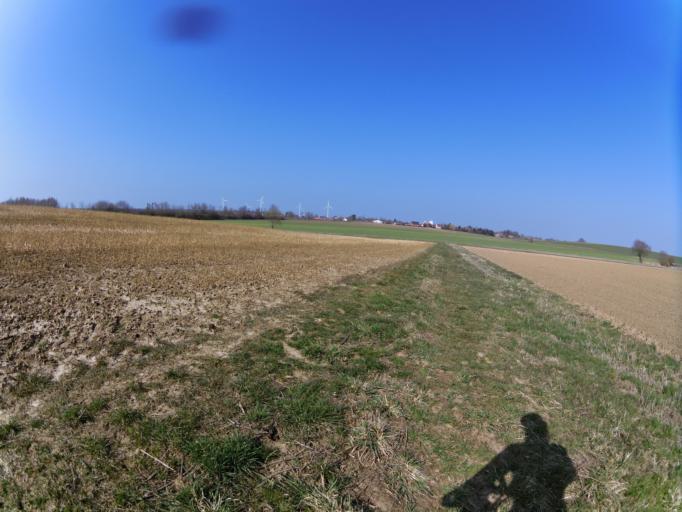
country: DE
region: Bavaria
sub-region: Regierungsbezirk Unterfranken
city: Geroldshausen
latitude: 49.6757
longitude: 9.9049
